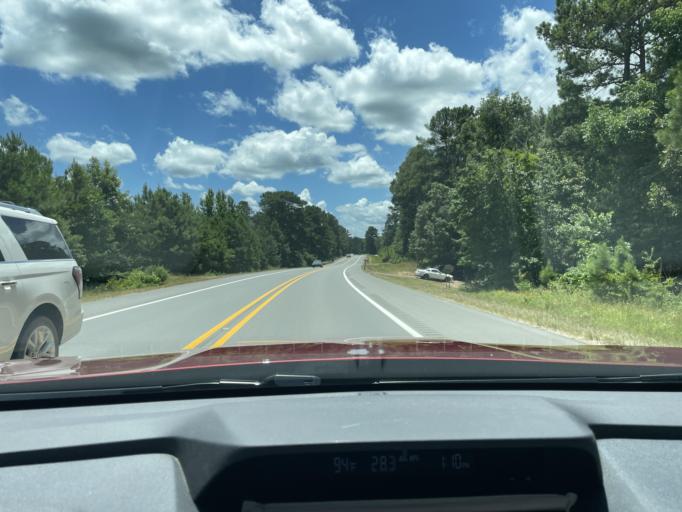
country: US
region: Arkansas
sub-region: Drew County
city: Monticello
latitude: 33.7203
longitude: -91.8103
